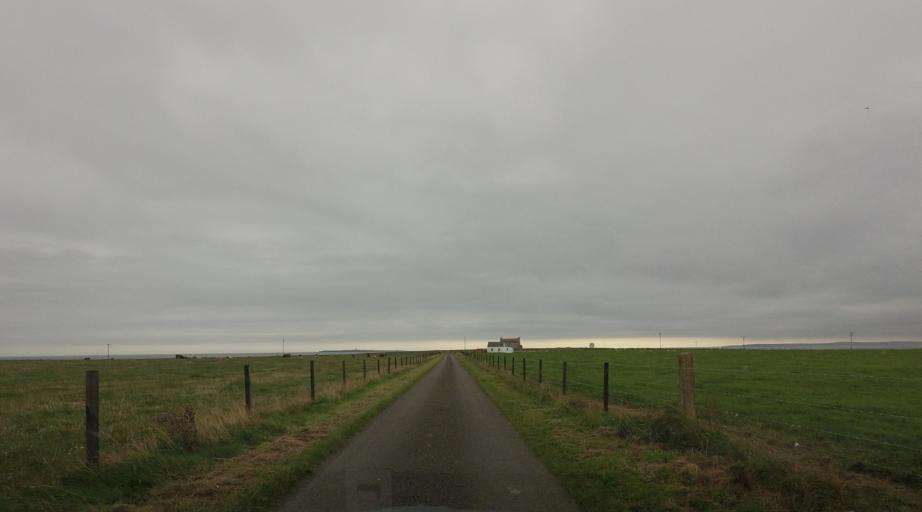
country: GB
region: Scotland
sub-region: Orkney Islands
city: Orkney
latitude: 58.7369
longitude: -2.9589
